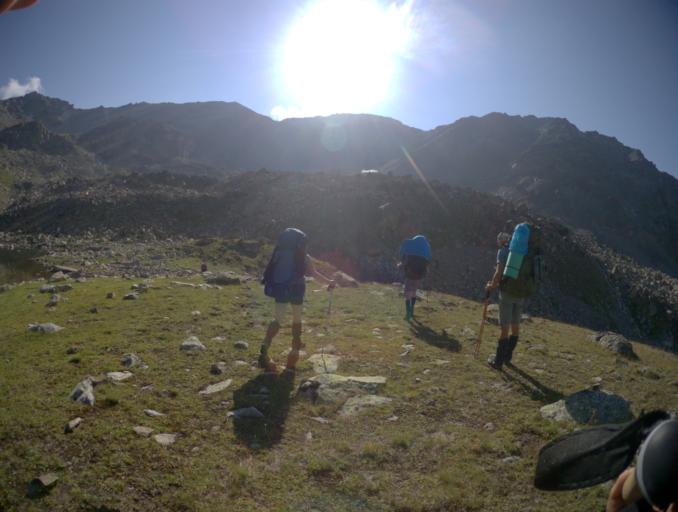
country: RU
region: Karachayevo-Cherkesiya
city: Uchkulan
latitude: 43.3126
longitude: 42.0673
